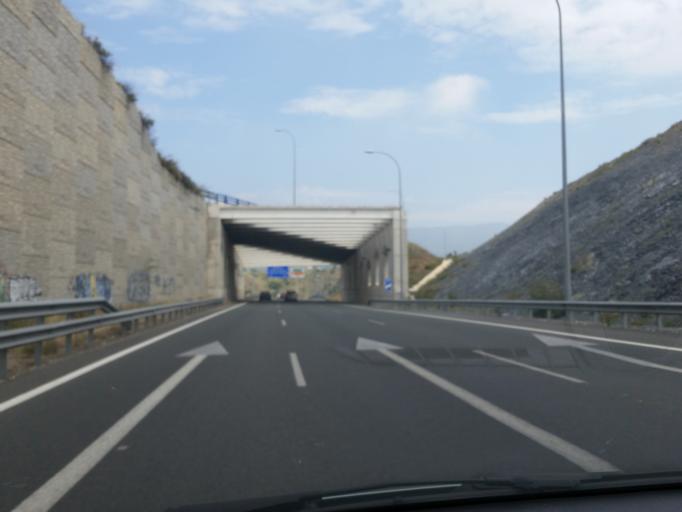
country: ES
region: Andalusia
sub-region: Provincia de Malaga
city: Malaga
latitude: 36.7435
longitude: -4.4439
